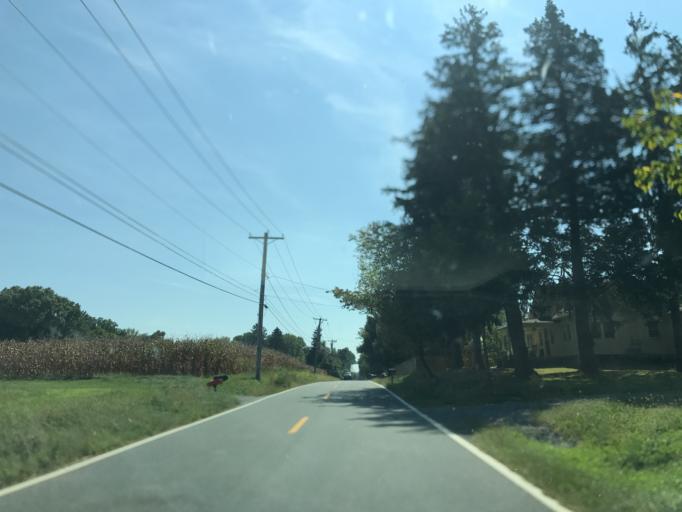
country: US
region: Maryland
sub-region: Cecil County
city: Elkton
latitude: 39.5171
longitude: -75.8137
